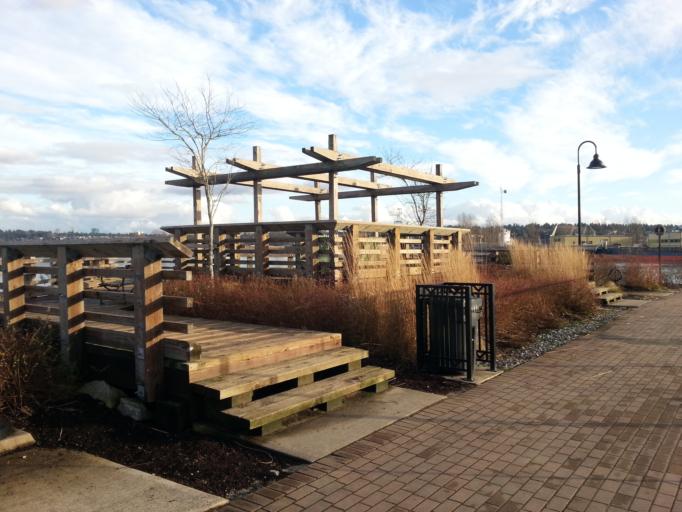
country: CA
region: British Columbia
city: New Westminster
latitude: 49.1956
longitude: -122.9214
